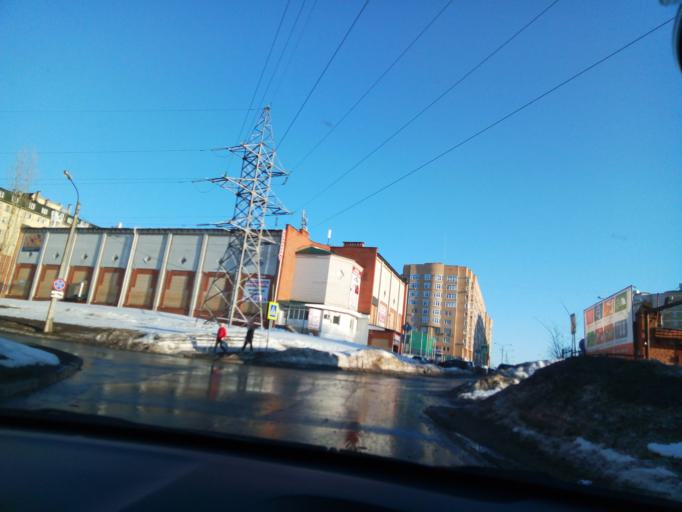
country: RU
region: Chuvashia
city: Novyye Lapsary
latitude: 56.1350
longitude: 47.1581
